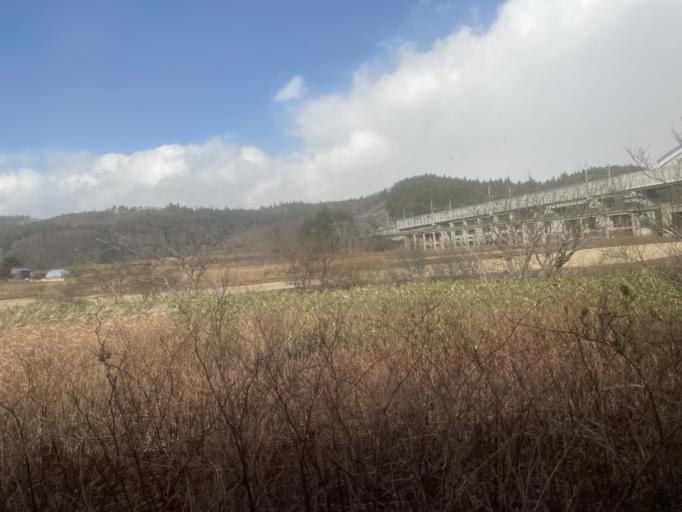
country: JP
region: Aomori
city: Goshogawara
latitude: 41.0658
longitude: 140.5608
